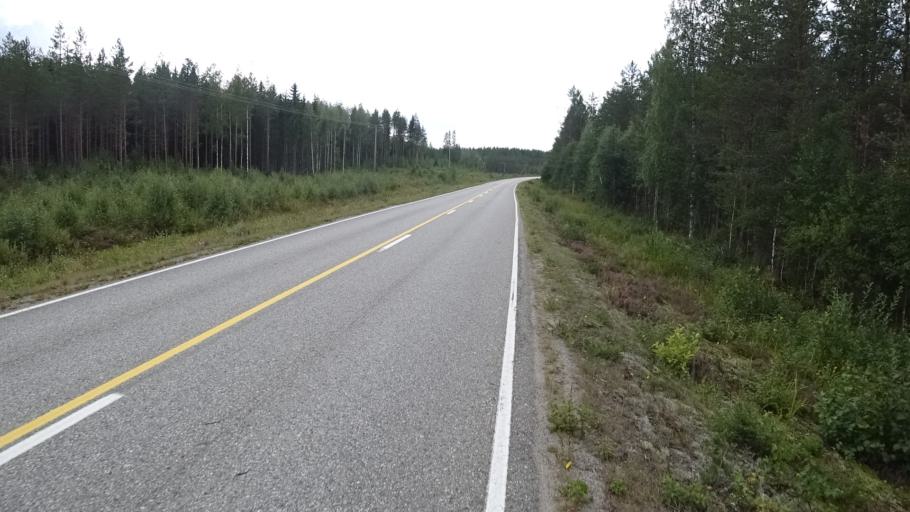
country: FI
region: North Karelia
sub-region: Joensuu
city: Ilomantsi
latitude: 62.6237
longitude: 31.2399
